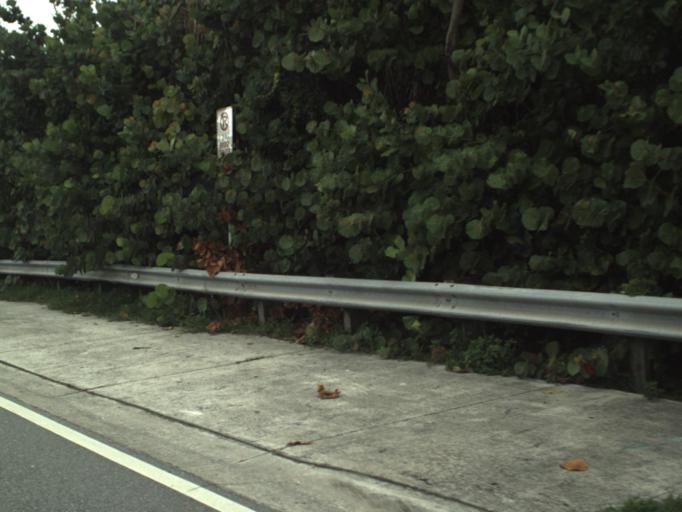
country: US
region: Florida
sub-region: Palm Beach County
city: Jupiter
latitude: 26.9491
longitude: -80.0852
